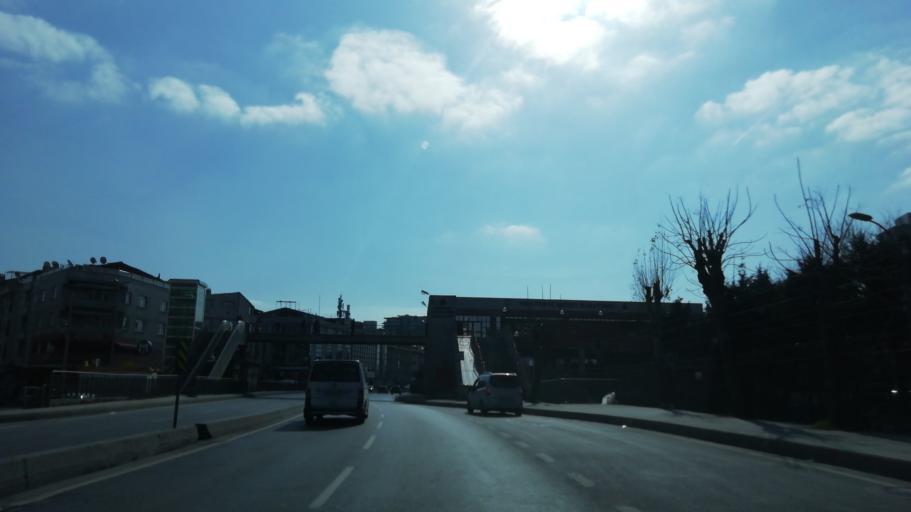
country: TR
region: Istanbul
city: merter keresteciler
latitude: 41.0312
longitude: 28.8975
